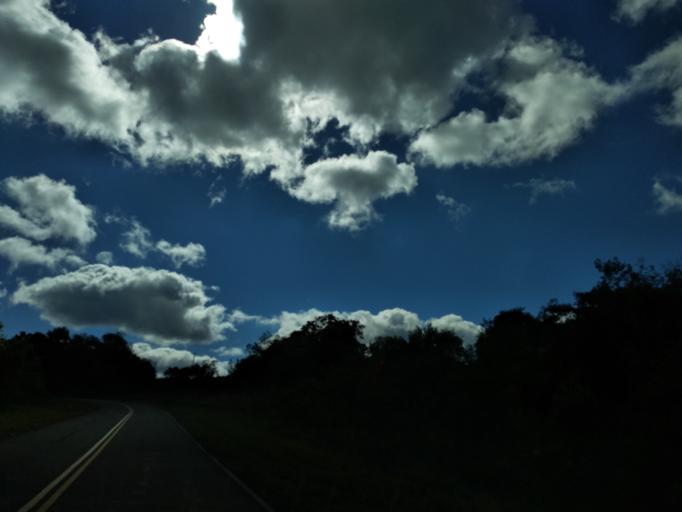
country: AR
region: Misiones
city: Santa Ana
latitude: -27.4230
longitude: -55.5673
